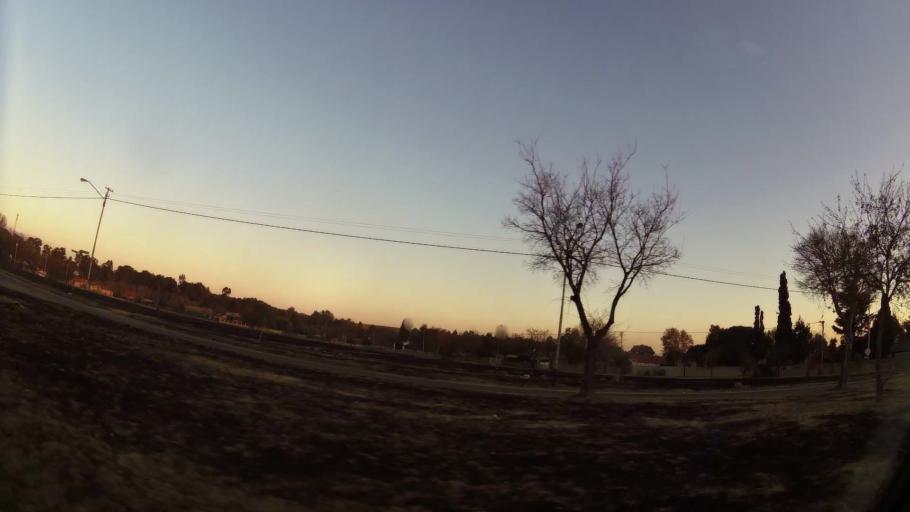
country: ZA
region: Gauteng
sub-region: Ekurhuleni Metropolitan Municipality
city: Germiston
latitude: -26.2743
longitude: 28.1524
